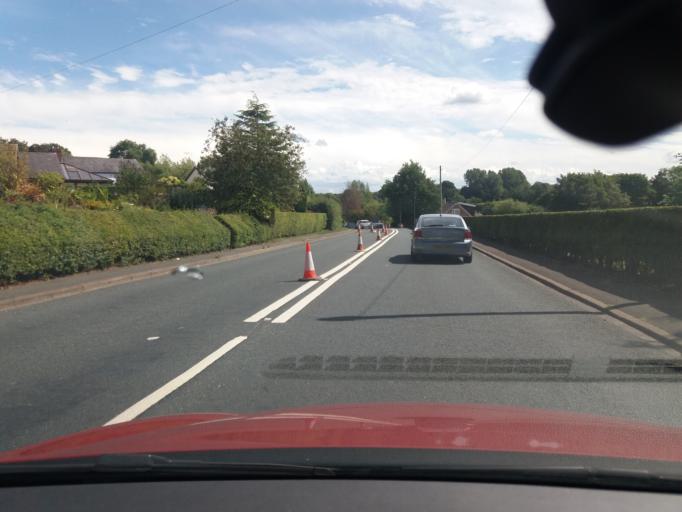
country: GB
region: England
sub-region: Lancashire
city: Euxton
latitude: 53.6581
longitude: -2.6865
